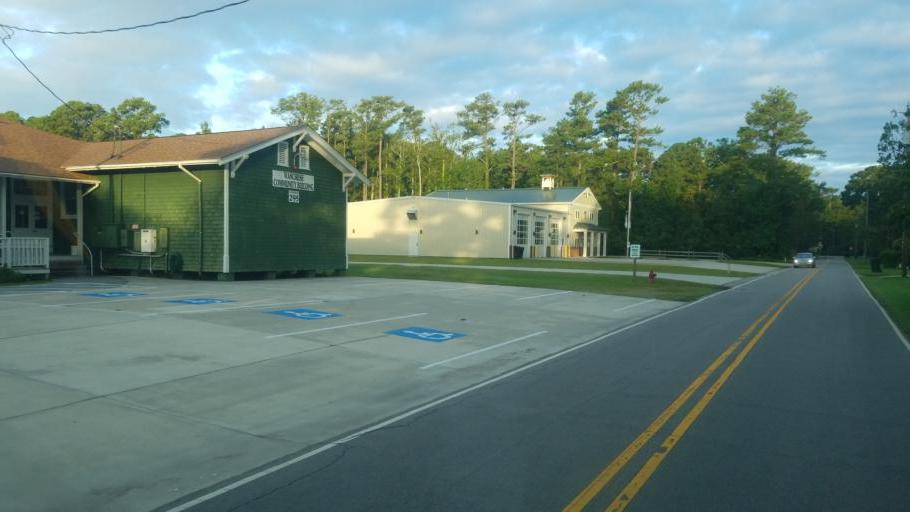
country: US
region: North Carolina
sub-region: Dare County
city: Wanchese
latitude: 35.8429
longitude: -75.6399
